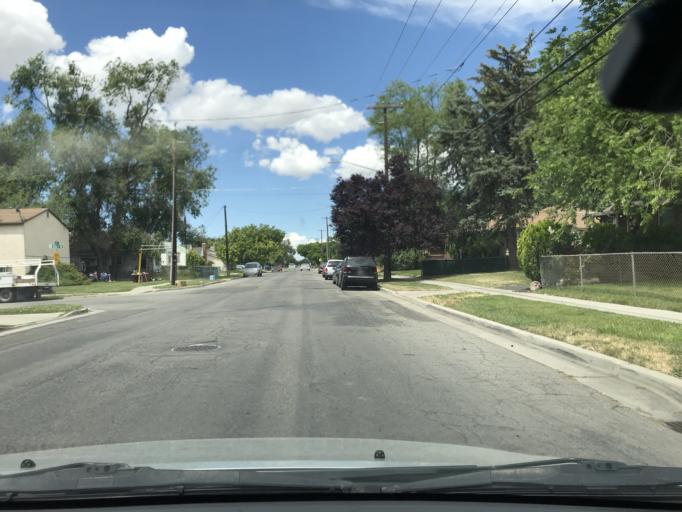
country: US
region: Utah
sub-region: Salt Lake County
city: Salt Lake City
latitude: 40.7802
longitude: -111.9324
